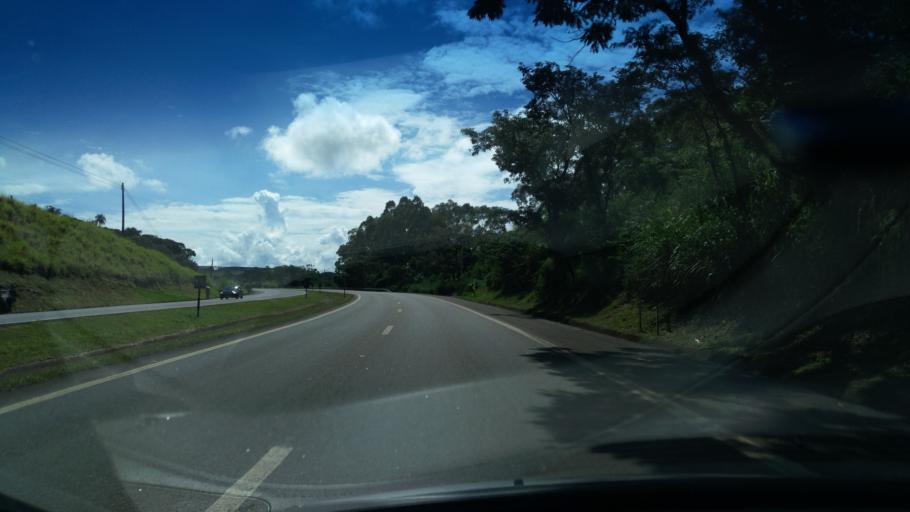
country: BR
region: Sao Paulo
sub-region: Santo Antonio Do Jardim
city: Espirito Santo do Pinhal
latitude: -22.2188
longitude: -46.7867
